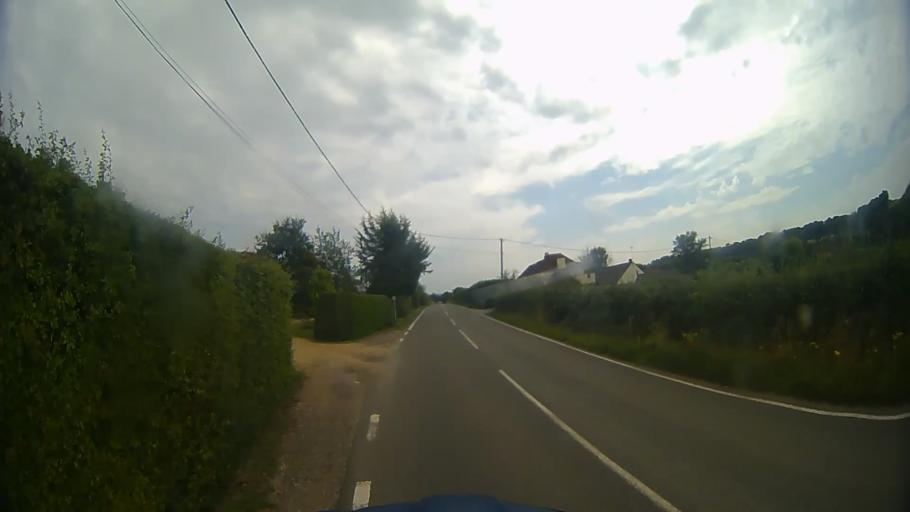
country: GB
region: England
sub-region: Hampshire
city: Kingsley
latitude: 51.1745
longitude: -0.8677
